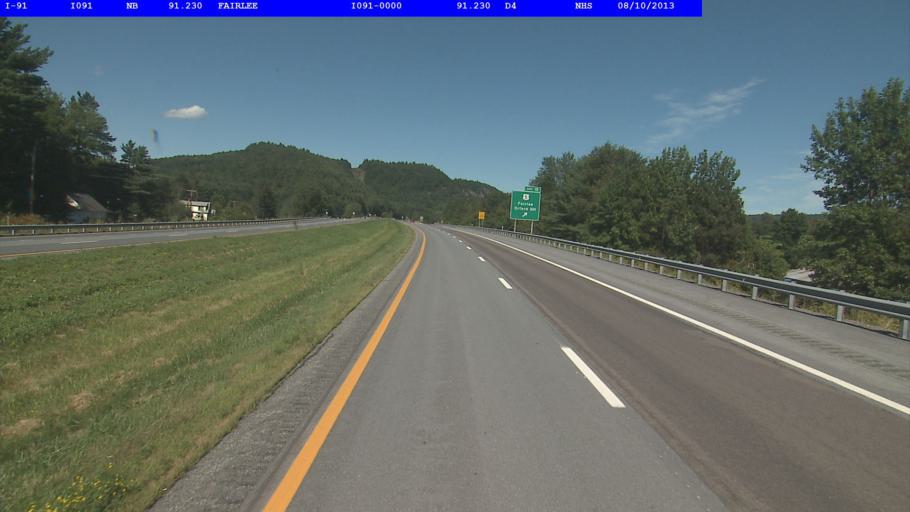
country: US
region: New Hampshire
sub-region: Grafton County
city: Orford
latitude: 43.9020
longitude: -72.1559
